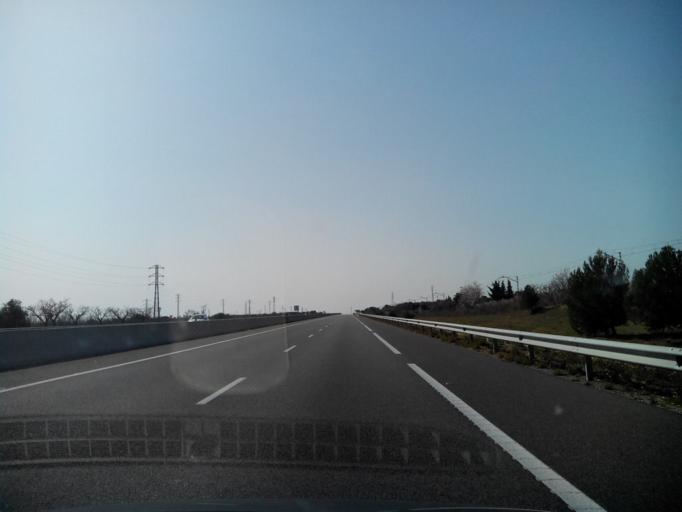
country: ES
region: Catalonia
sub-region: Provincia de Tarragona
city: Alcover
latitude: 41.2376
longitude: 1.1656
